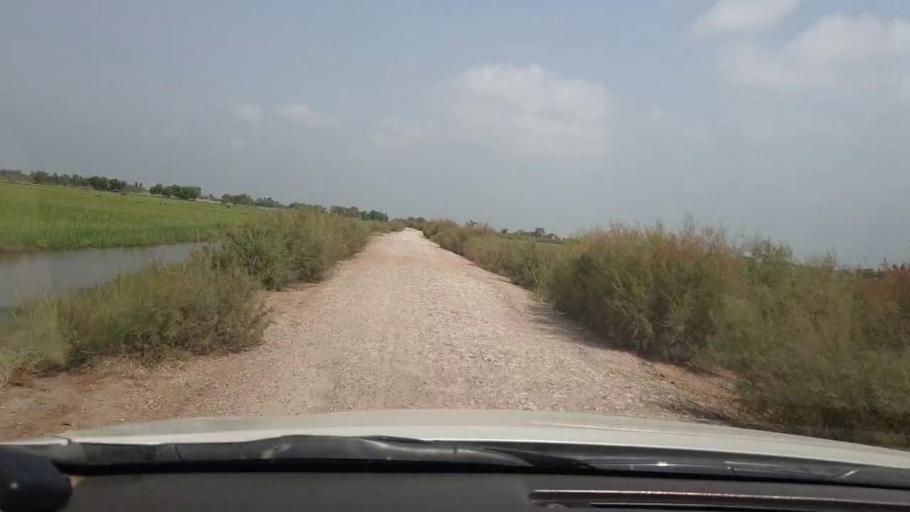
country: PK
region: Sindh
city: Garhi Yasin
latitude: 28.0051
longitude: 68.5403
